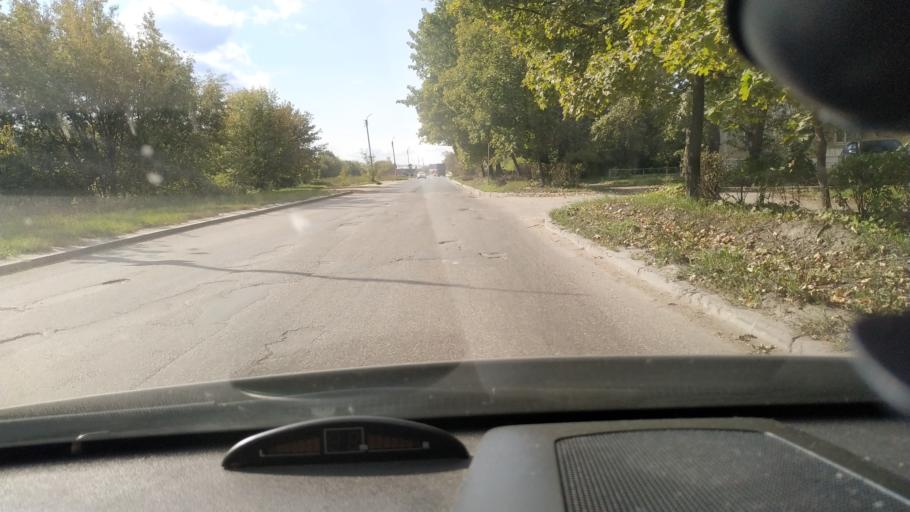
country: RU
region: Rjazan
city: Ryazan'
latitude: 54.6512
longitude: 39.6485
